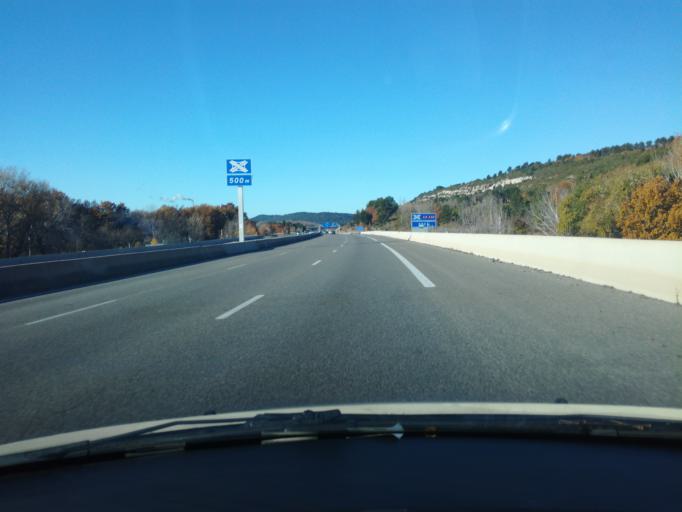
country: FR
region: Provence-Alpes-Cote d'Azur
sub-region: Departement des Bouches-du-Rhone
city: Chateauneuf-le-Rouge
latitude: 43.4813
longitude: 5.5718
